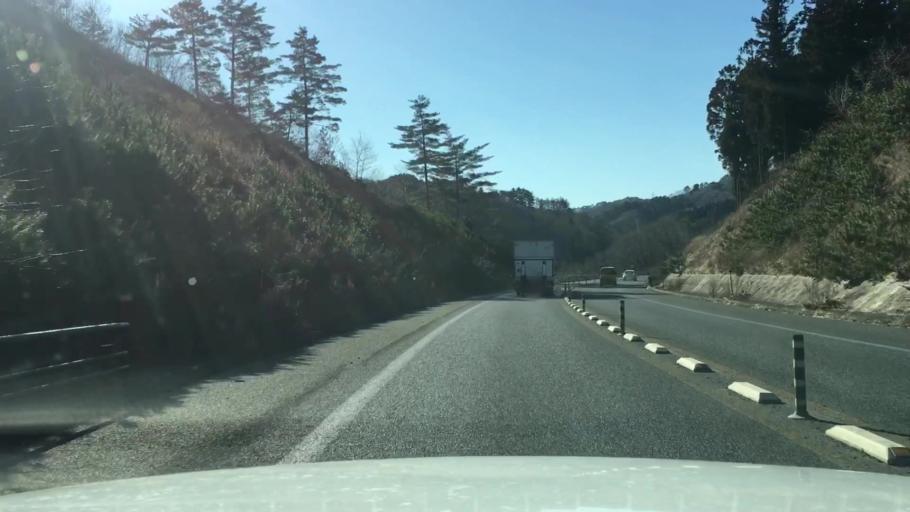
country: JP
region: Iwate
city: Miyako
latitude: 39.6126
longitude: 141.9349
